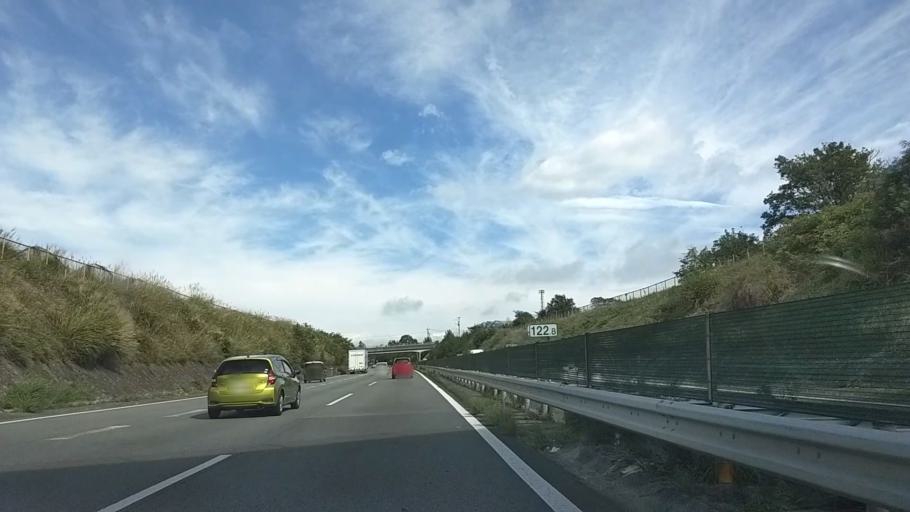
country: JP
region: Yamanashi
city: Nirasaki
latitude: 35.7084
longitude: 138.4740
